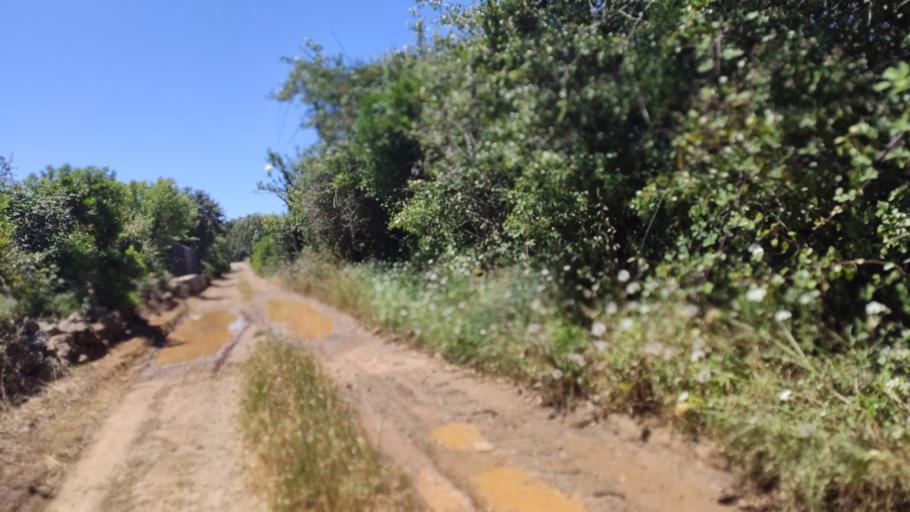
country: PT
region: Faro
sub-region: Sao Bras de Alportel
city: Sao Bras de Alportel
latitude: 37.1629
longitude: -7.9314
